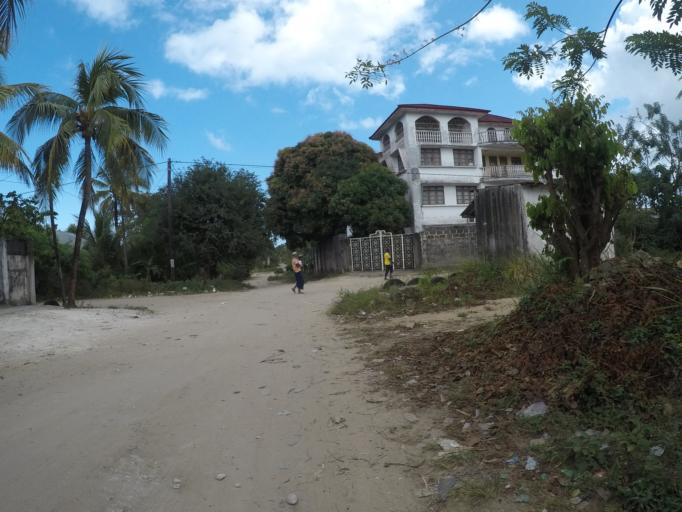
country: TZ
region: Zanzibar Urban/West
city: Zanzibar
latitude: -6.1873
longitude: 39.2164
